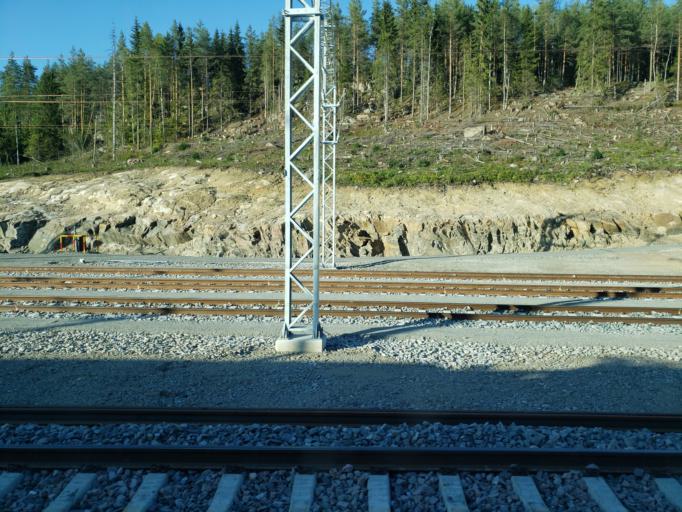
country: FI
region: South Karelia
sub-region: Lappeenranta
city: Lappeenranta
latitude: 60.8593
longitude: 28.3229
